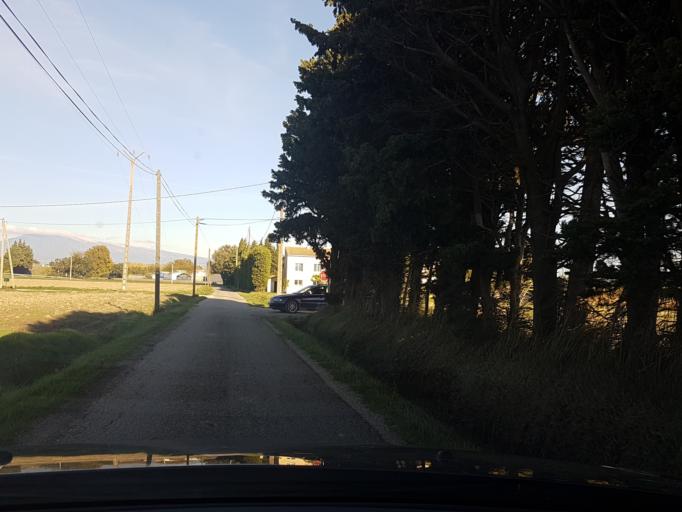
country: FR
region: Provence-Alpes-Cote d'Azur
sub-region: Departement du Vaucluse
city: Monteux
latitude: 44.0352
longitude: 4.9667
